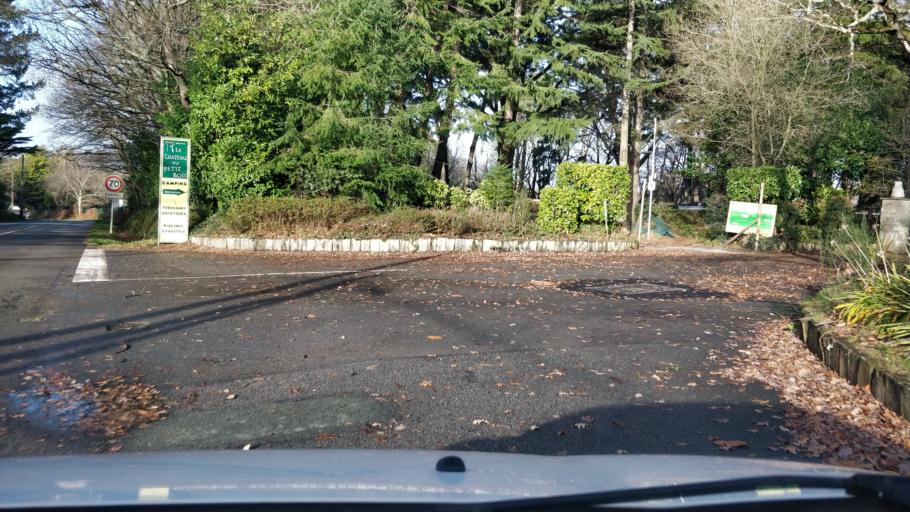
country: FR
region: Pays de la Loire
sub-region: Departement de la Loire-Atlantique
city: Mesquer
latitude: 47.3970
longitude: -2.4719
